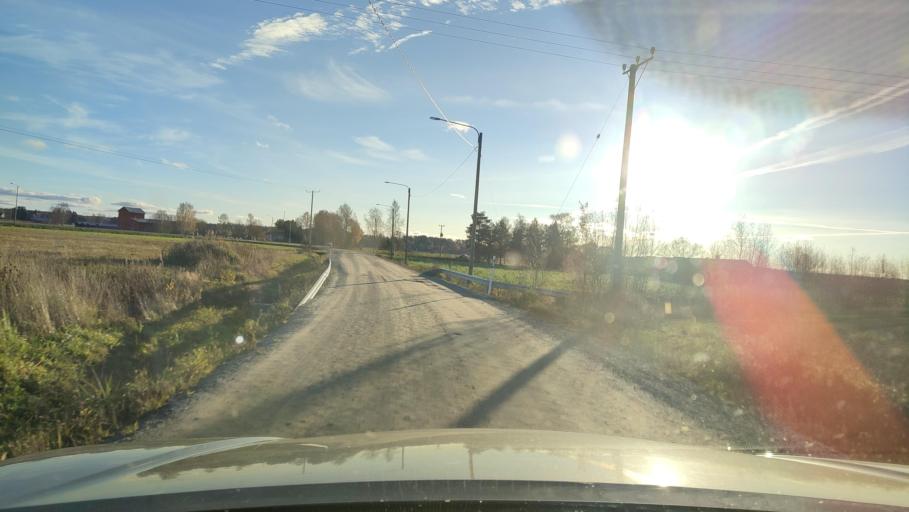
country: FI
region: Ostrobothnia
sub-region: Vaasa
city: Teeriniemi
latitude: 63.0109
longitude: 21.6929
